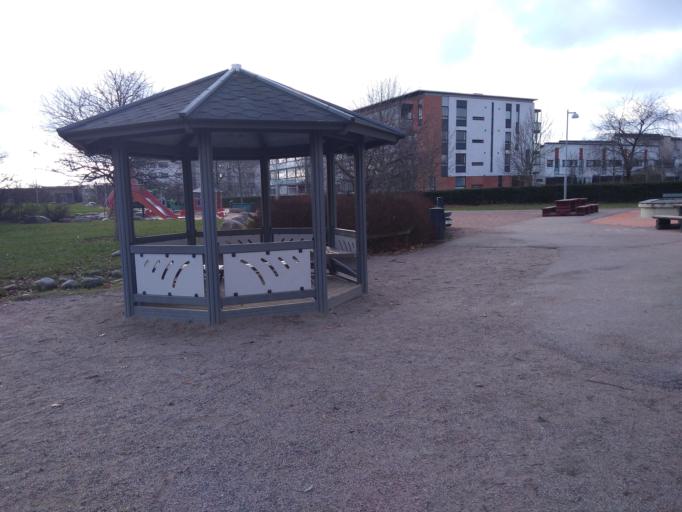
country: FI
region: Uusimaa
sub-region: Helsinki
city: Vantaa
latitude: 60.2299
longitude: 25.0335
